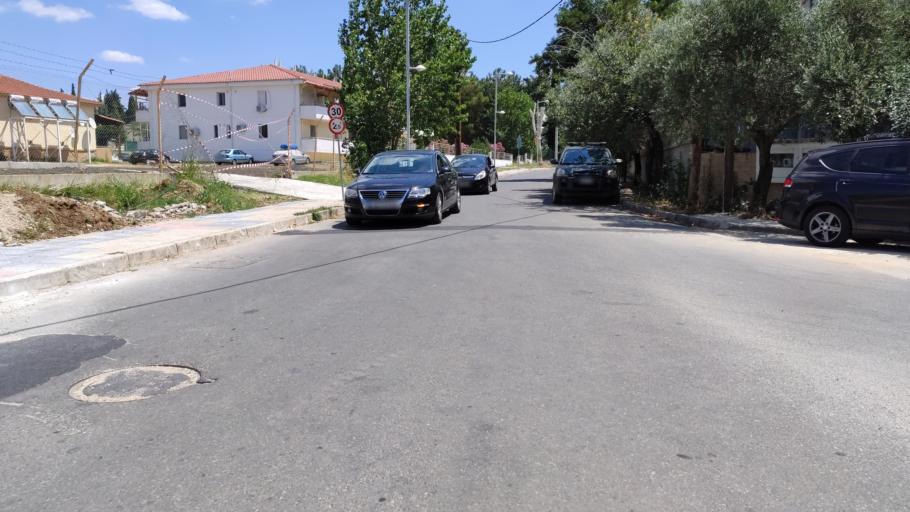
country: GR
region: East Macedonia and Thrace
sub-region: Nomos Rodopis
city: Komotini
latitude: 41.1298
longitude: 25.4078
